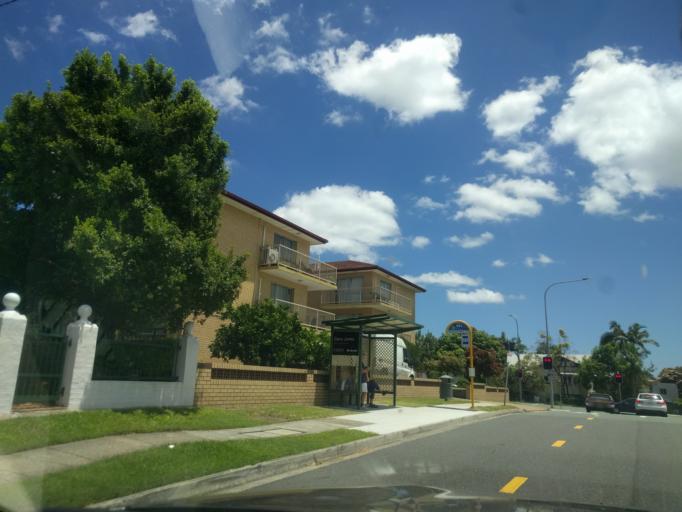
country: AU
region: Queensland
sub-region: Brisbane
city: Gordon Park
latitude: -27.4124
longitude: 153.0273
